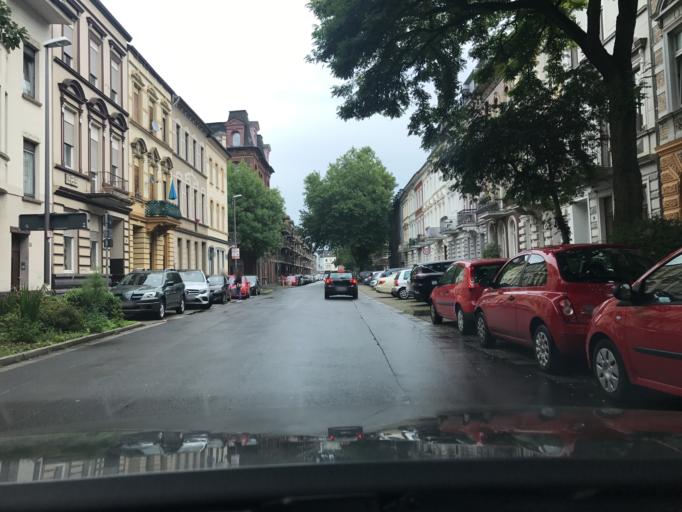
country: DE
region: North Rhine-Westphalia
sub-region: Regierungsbezirk Dusseldorf
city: Krefeld
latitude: 51.3216
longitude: 6.5658
